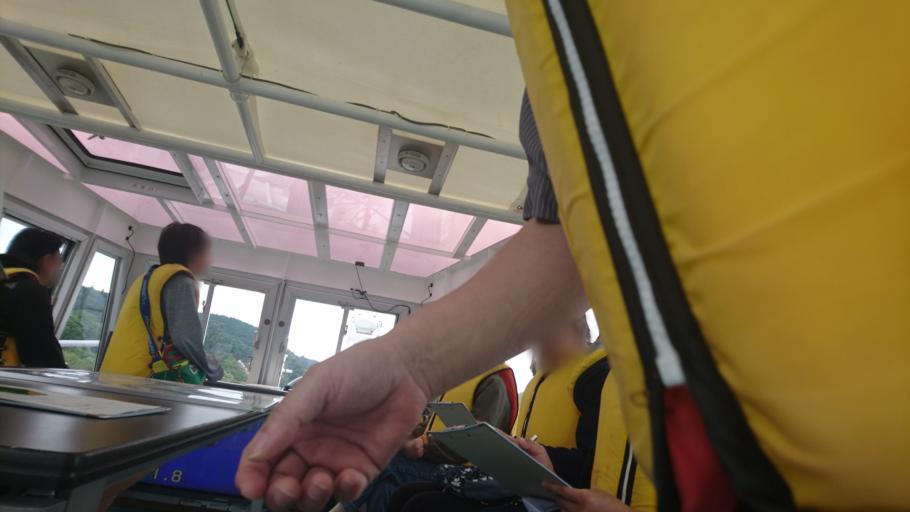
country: JP
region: Iwate
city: Ichinoseki
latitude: 38.9009
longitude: 141.2602
